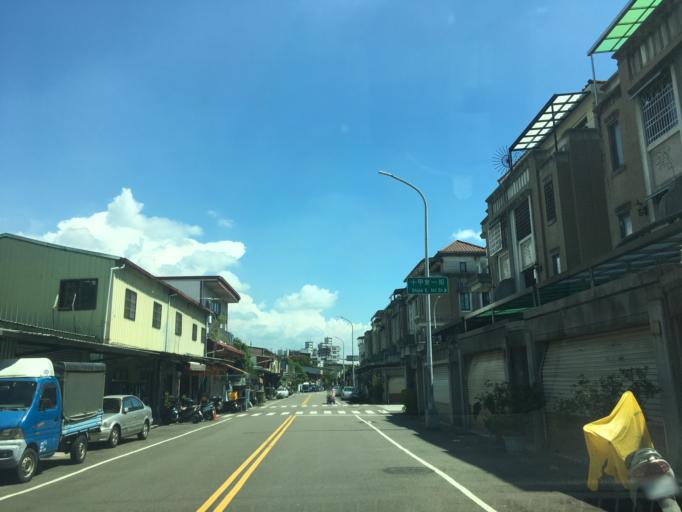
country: TW
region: Taiwan
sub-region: Taichung City
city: Taichung
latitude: 24.1473
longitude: 120.7116
